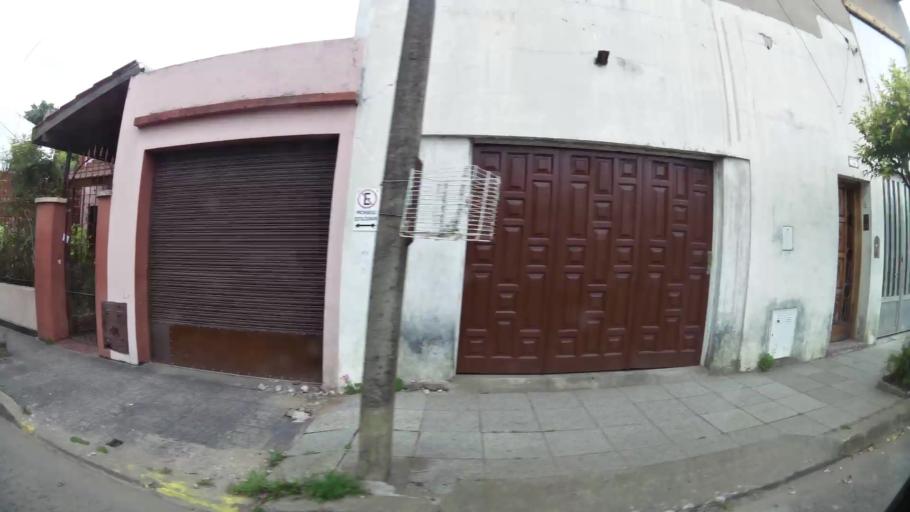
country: AR
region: Buenos Aires
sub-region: Partido de Zarate
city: Zarate
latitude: -34.1083
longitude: -59.0145
